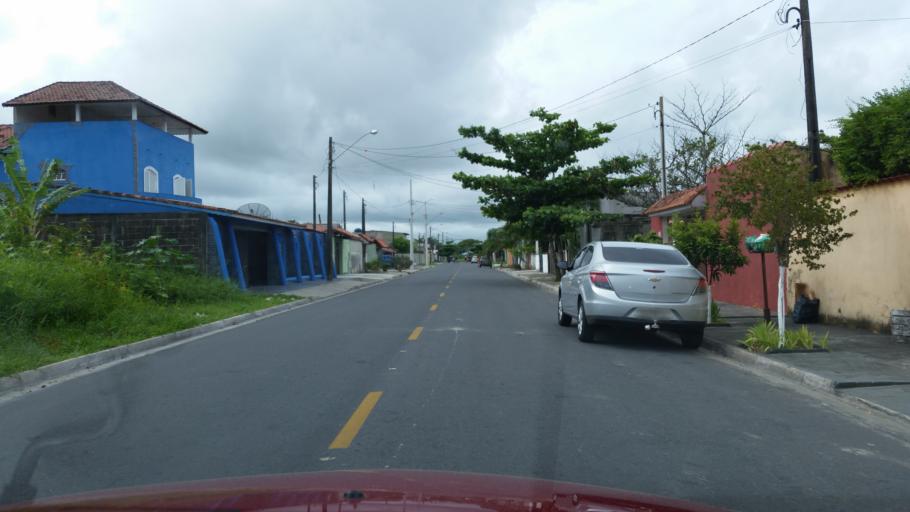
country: BR
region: Sao Paulo
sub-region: Iguape
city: Iguape
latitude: -24.7441
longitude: -47.5548
